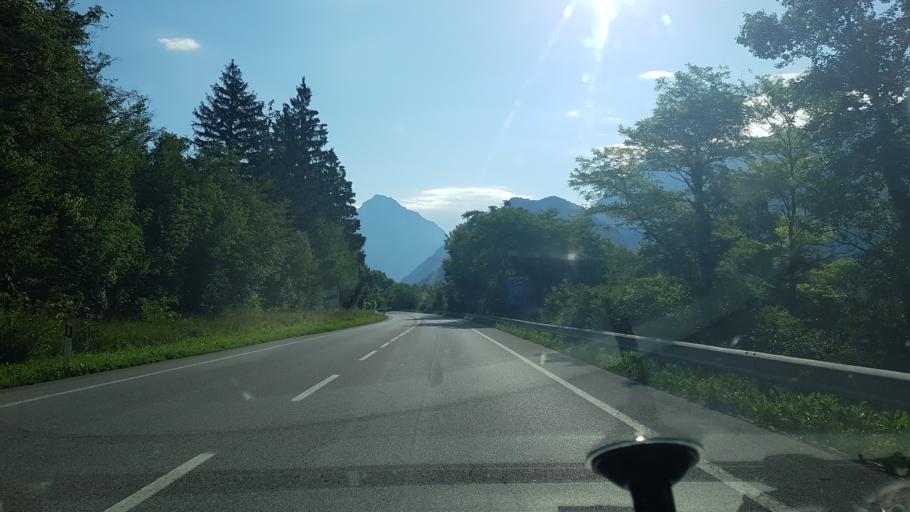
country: IT
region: Friuli Venezia Giulia
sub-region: Provincia di Udine
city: Amaro
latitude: 46.3777
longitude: 13.1092
